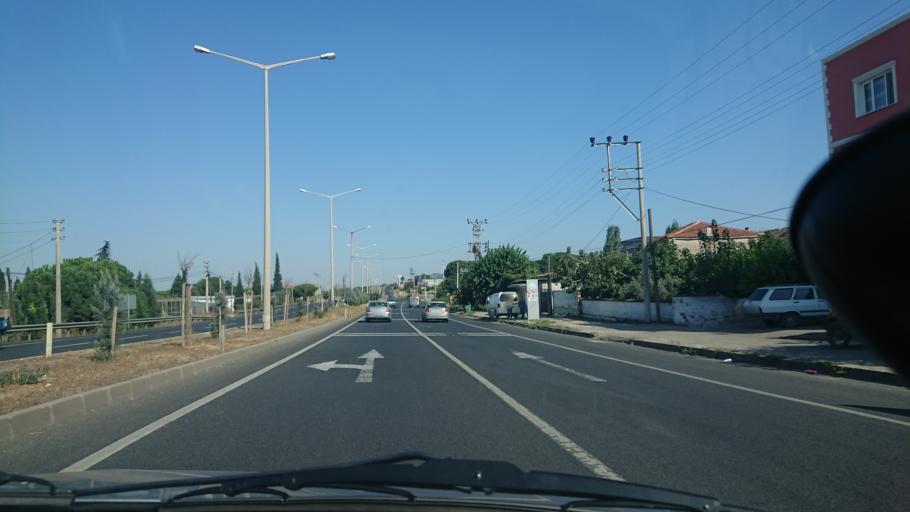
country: TR
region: Manisa
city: Turgutlu
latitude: 38.4954
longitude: 27.7666
